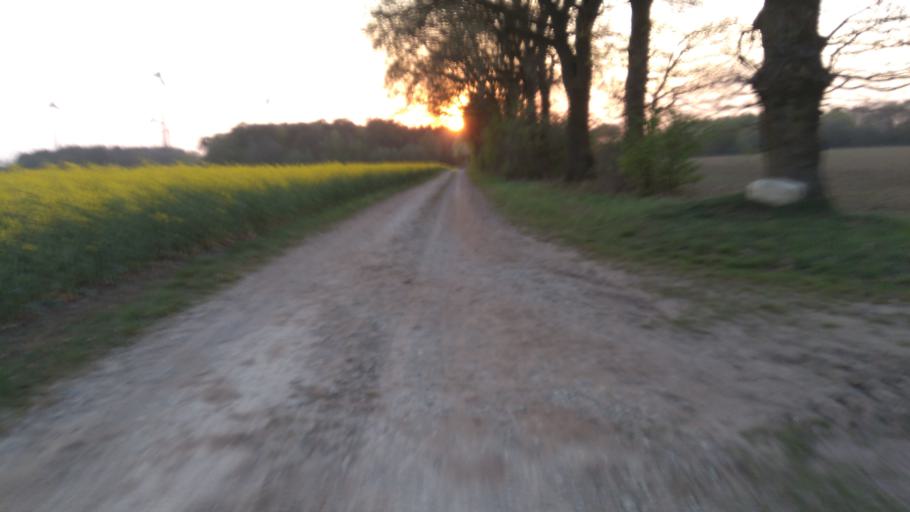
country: DE
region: Lower Saxony
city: Harsefeld
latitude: 53.4939
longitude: 9.5047
